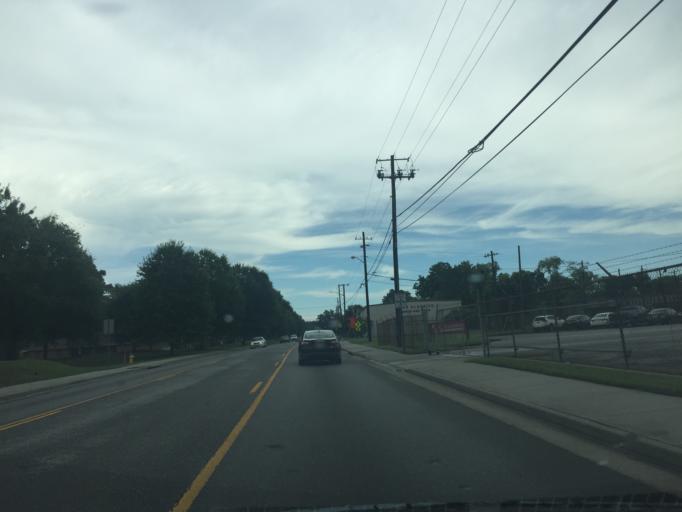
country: US
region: Georgia
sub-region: Chatham County
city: Savannah
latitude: 32.0681
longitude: -81.0813
